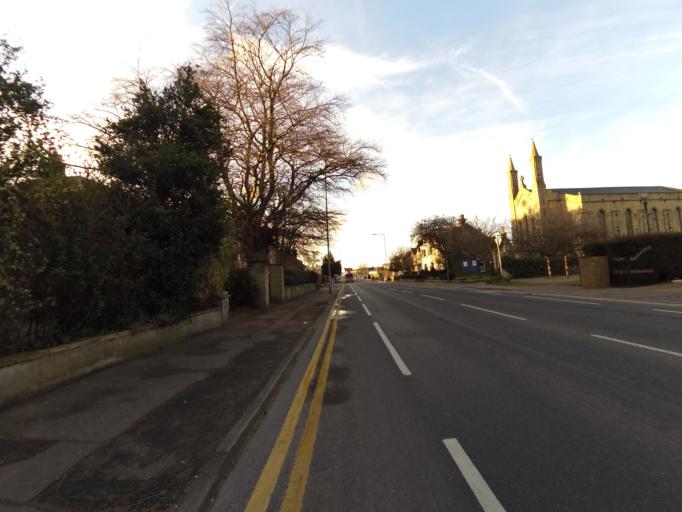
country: GB
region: England
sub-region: Norfolk
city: Great Yarmouth
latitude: 52.6032
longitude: 1.7220
